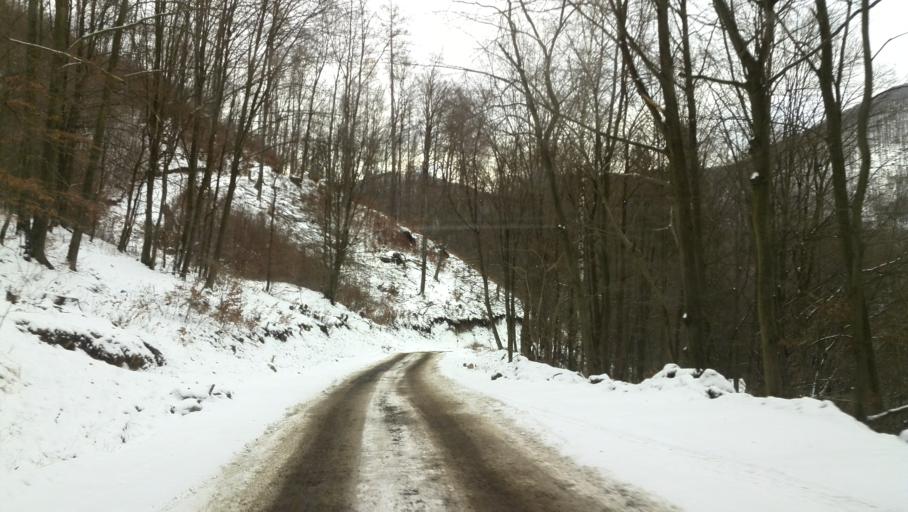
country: SK
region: Kosicky
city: Gelnica
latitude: 48.8154
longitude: 21.0658
